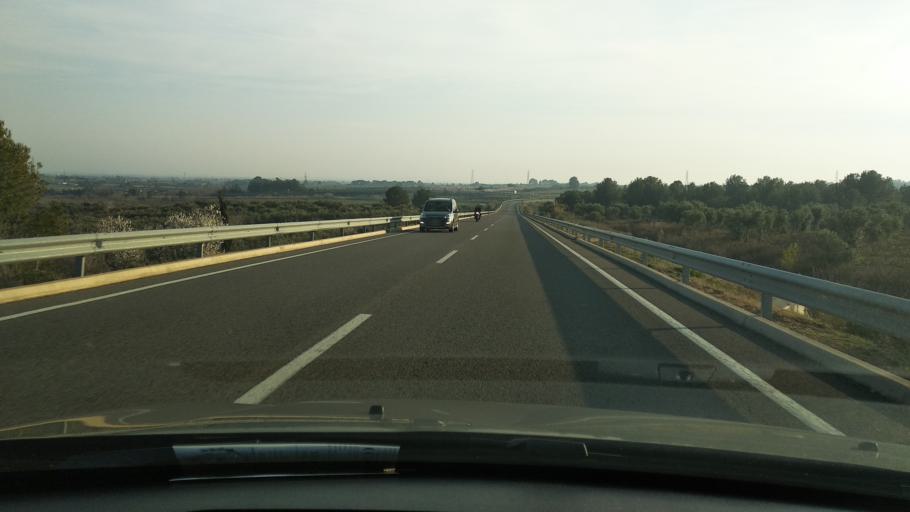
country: ES
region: Catalonia
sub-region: Provincia de Tarragona
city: les Borges del Camp
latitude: 41.1697
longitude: 1.0097
